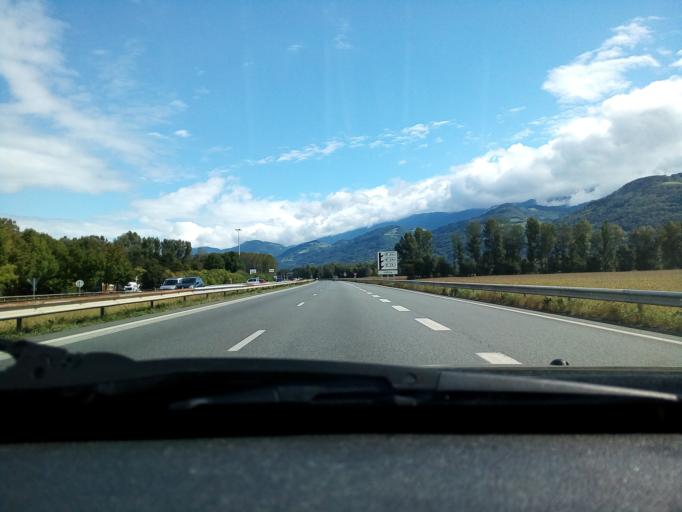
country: FR
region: Rhone-Alpes
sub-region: Departement de l'Isere
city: Saint-Nazaire-les-Eymes
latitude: 45.2457
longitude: 5.8653
